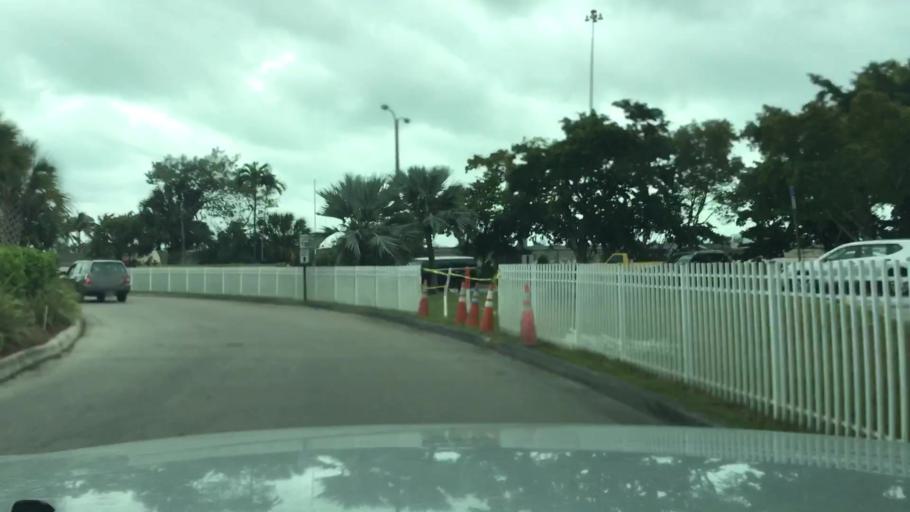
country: US
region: Florida
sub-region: Miami-Dade County
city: Miami Beach
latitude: 25.8113
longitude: -80.1431
